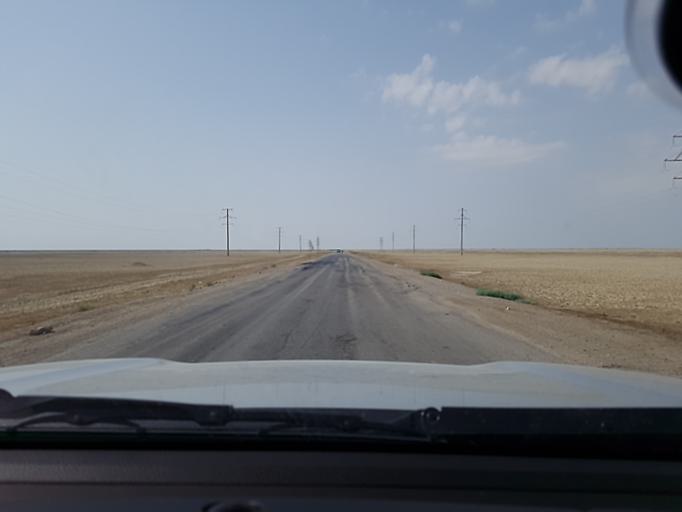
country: TM
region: Balkan
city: Gumdag
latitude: 39.0604
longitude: 54.5844
